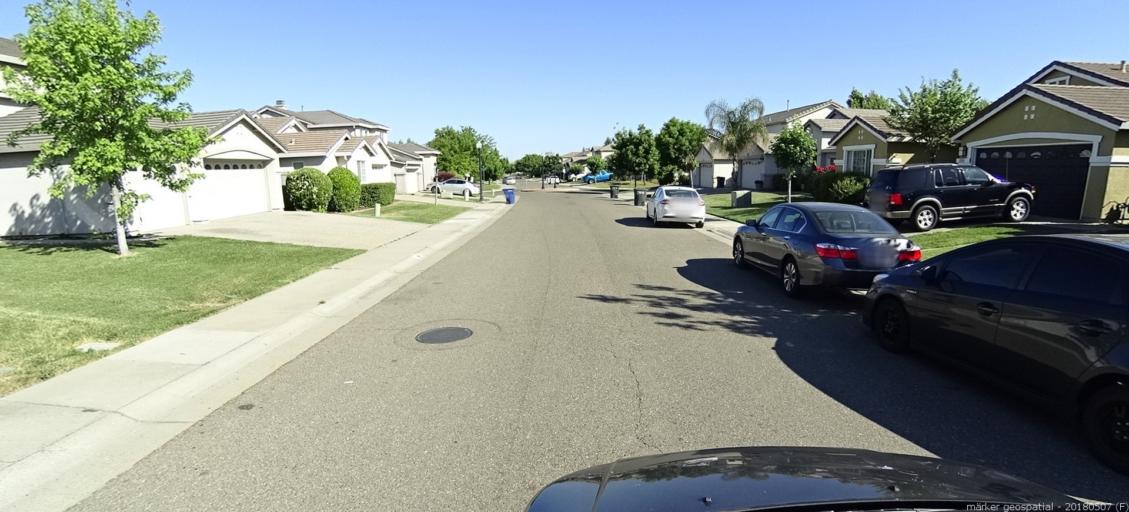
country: US
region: California
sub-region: Sacramento County
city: Rio Linda
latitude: 38.6729
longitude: -121.4978
